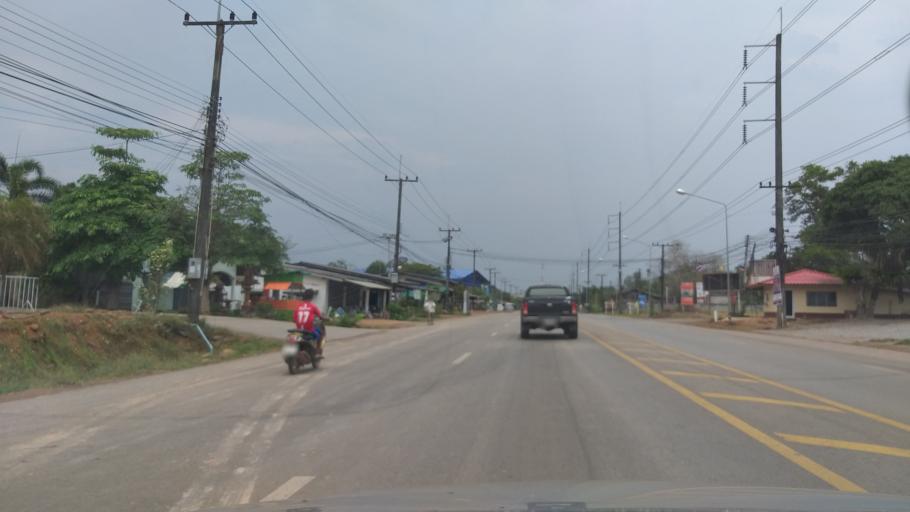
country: TH
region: Trat
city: Khao Saming
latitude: 12.3032
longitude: 102.3453
